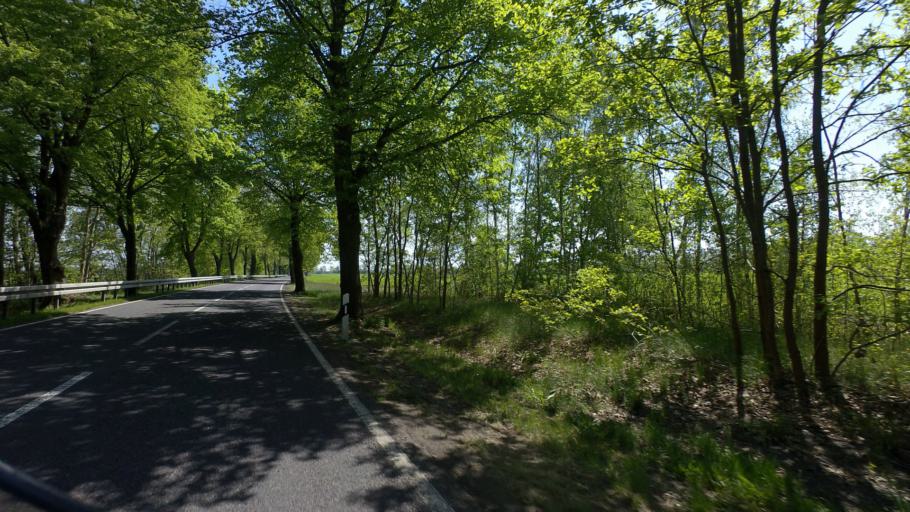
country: DE
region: Brandenburg
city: Munchehofe
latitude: 52.0943
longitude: 13.8465
